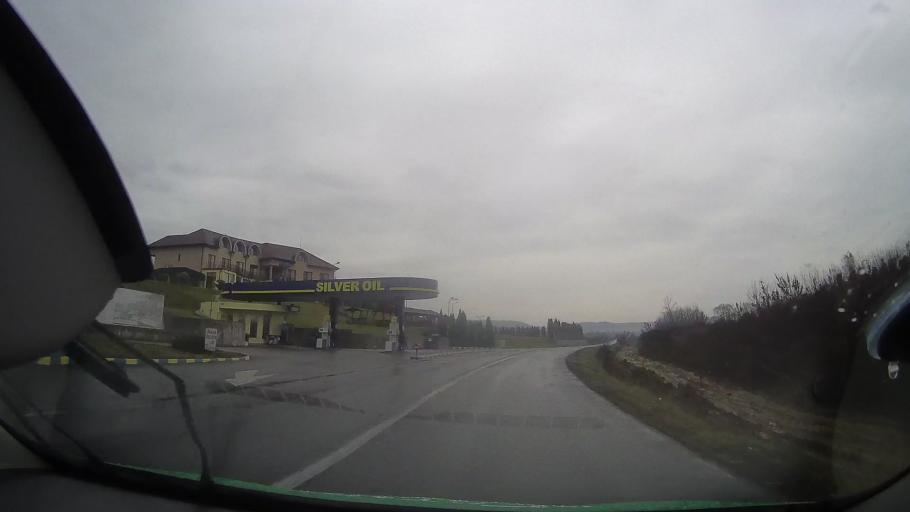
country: RO
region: Bihor
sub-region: Comuna Sambata
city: Sambata
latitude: 46.7896
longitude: 22.2039
